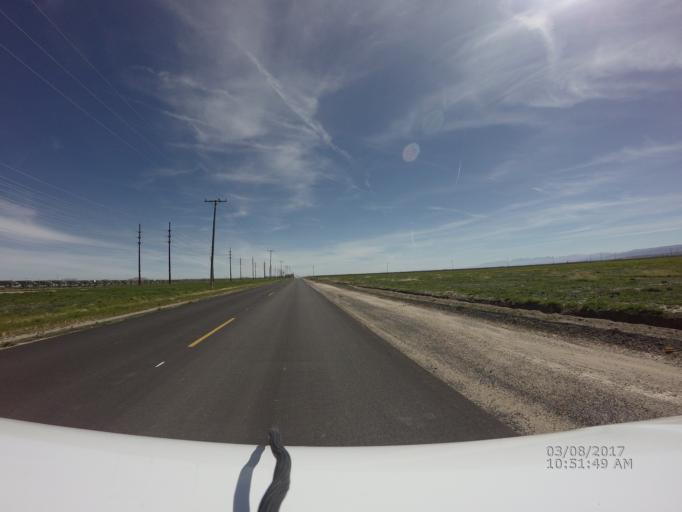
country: US
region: California
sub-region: Los Angeles County
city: Green Valley
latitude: 34.8190
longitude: -118.4040
